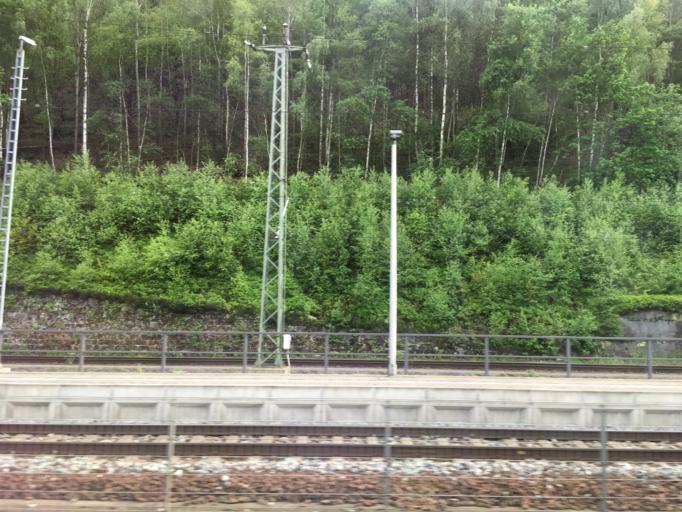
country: DE
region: Saxony
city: Rathmannsdorf
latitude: 50.9202
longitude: 14.1343
